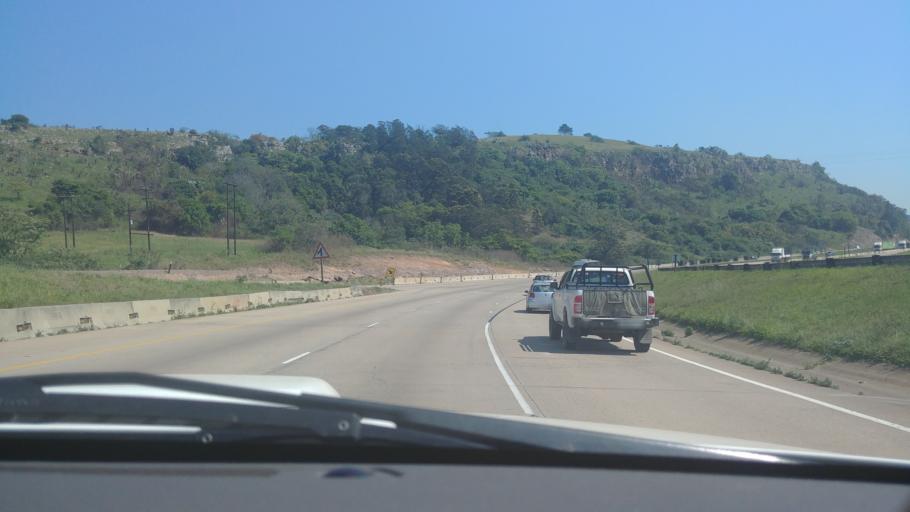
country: ZA
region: KwaZulu-Natal
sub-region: eThekwini Metropolitan Municipality
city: Mpumalanga
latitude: -29.7574
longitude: 30.6658
